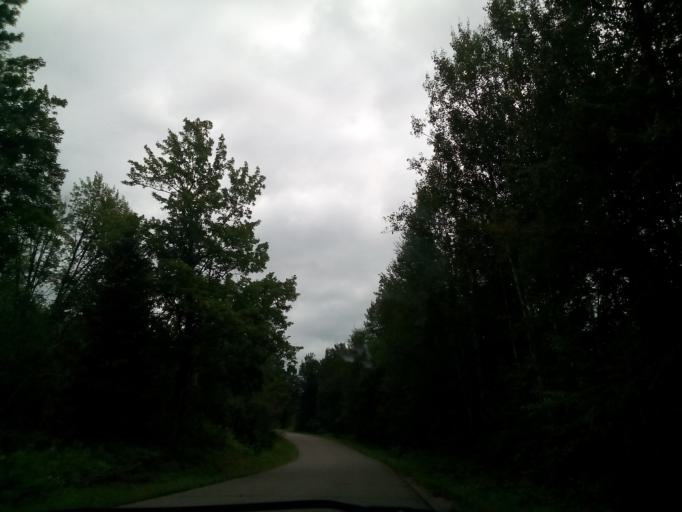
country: US
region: Wisconsin
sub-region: Menominee County
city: Legend Lake
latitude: 45.3248
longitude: -88.5277
